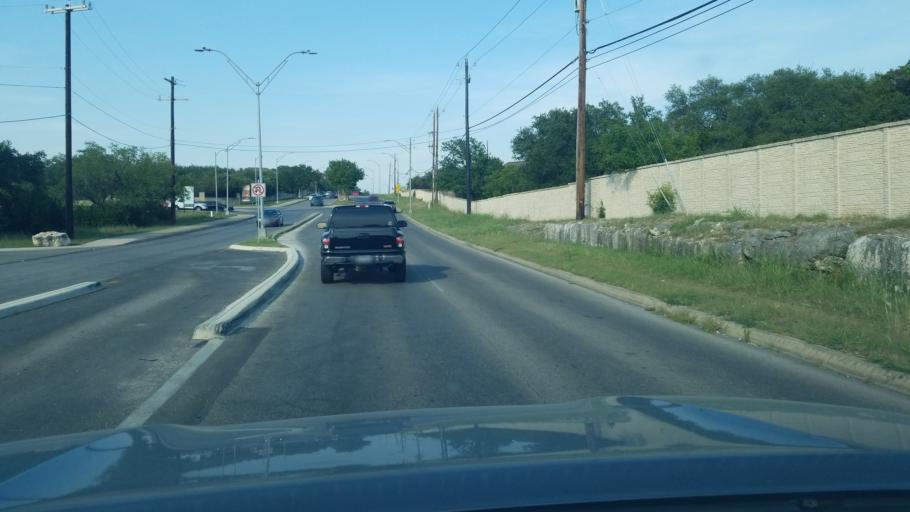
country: US
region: Texas
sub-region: Bexar County
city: Timberwood Park
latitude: 29.6623
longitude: -98.4989
